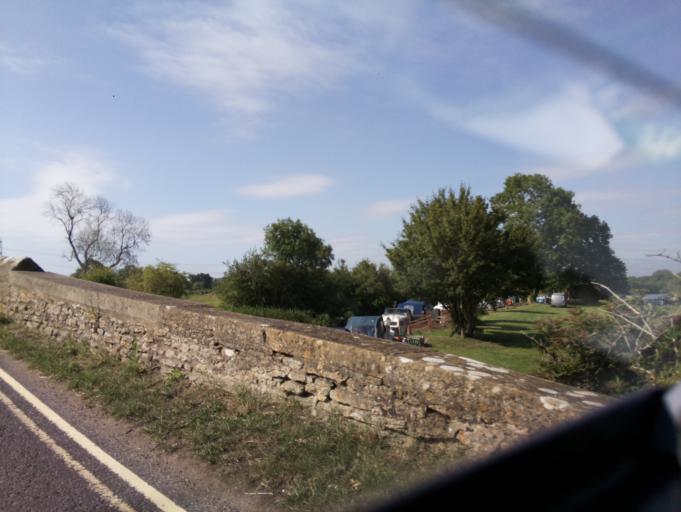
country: GB
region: England
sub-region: Oxfordshire
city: Faringdon
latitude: 51.6928
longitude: -1.5882
